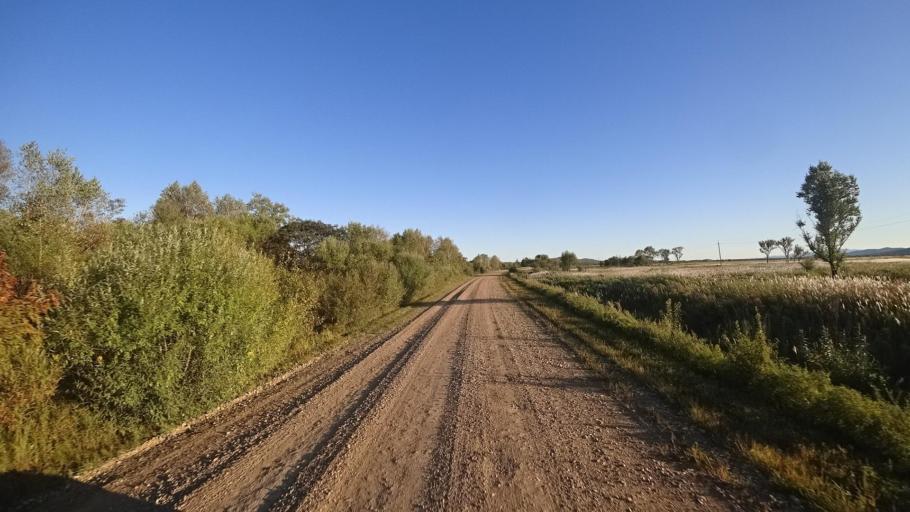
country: RU
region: Primorskiy
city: Kirovskiy
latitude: 44.8025
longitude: 133.6205
